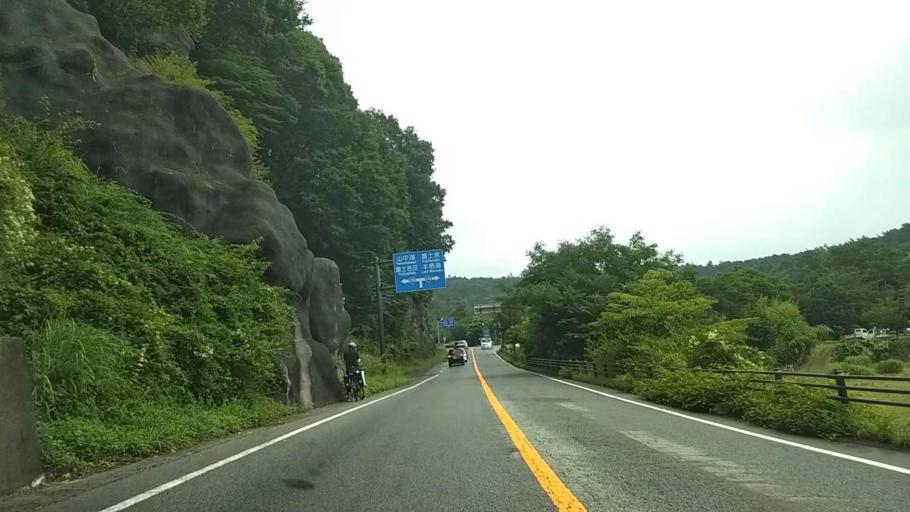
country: JP
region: Yamanashi
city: Fujikawaguchiko
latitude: 35.4859
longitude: 138.6176
